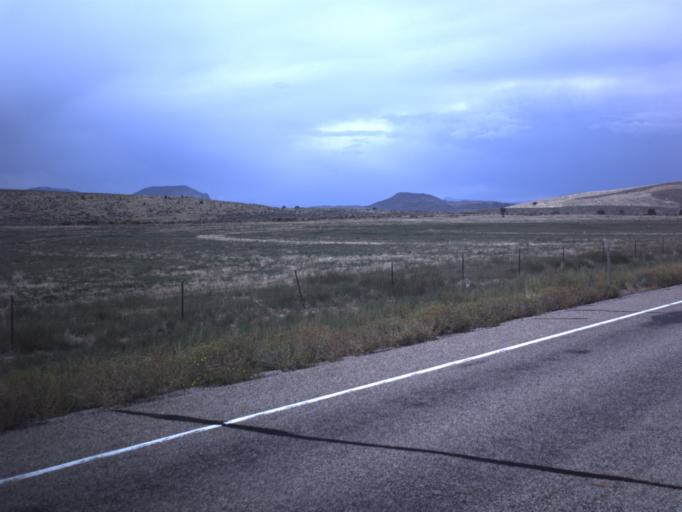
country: US
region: Utah
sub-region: Piute County
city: Junction
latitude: 38.1465
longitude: -112.2993
